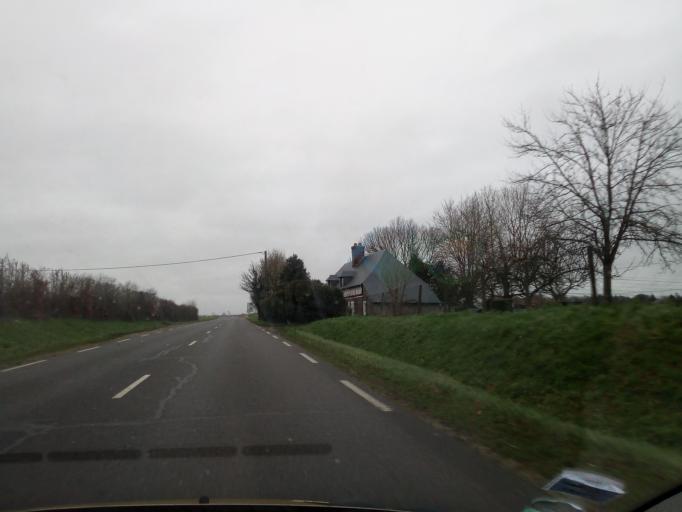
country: FR
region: Haute-Normandie
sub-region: Departement de la Seine-Maritime
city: Auzebosc
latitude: 49.5941
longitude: 0.7358
